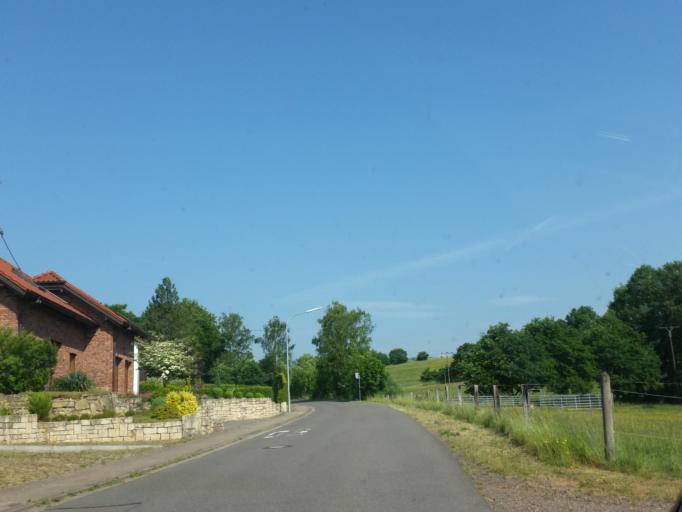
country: DE
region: Saarland
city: Weiskirchen
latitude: 49.5253
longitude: 6.8173
